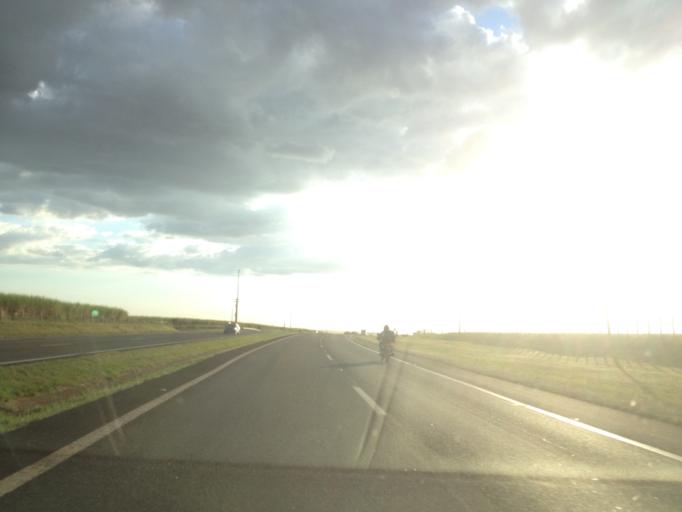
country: BR
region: Sao Paulo
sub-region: Jau
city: Jau
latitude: -22.2711
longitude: -48.4699
